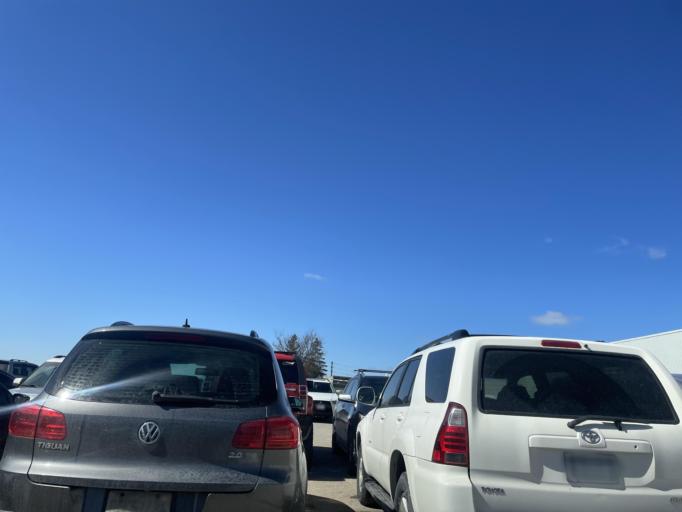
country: CA
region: Ontario
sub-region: Wellington County
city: Guelph
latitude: 43.5303
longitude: -80.3175
